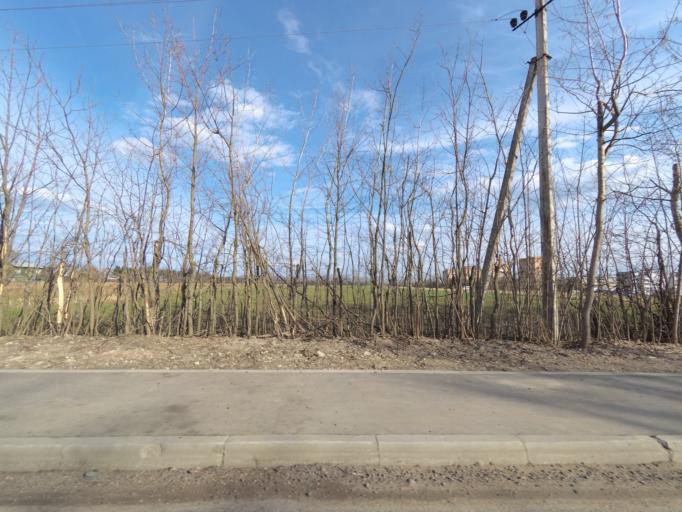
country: RU
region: Moskovskaya
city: Lugovaya
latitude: 56.0485
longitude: 37.4784
